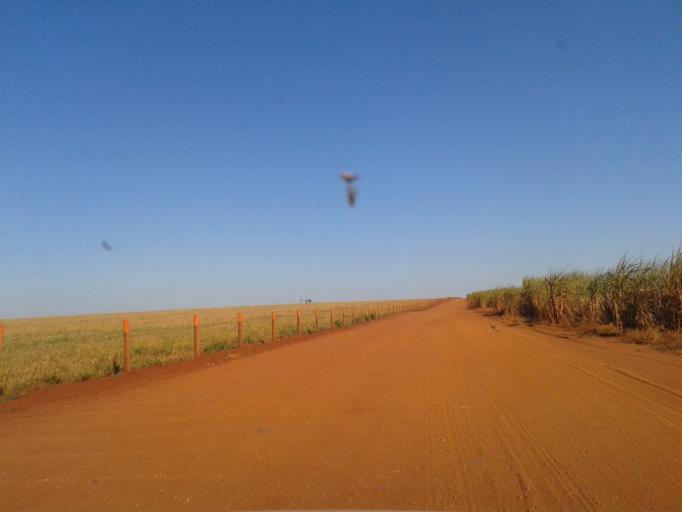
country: BR
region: Minas Gerais
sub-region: Santa Vitoria
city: Santa Vitoria
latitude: -18.8358
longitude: -50.0608
